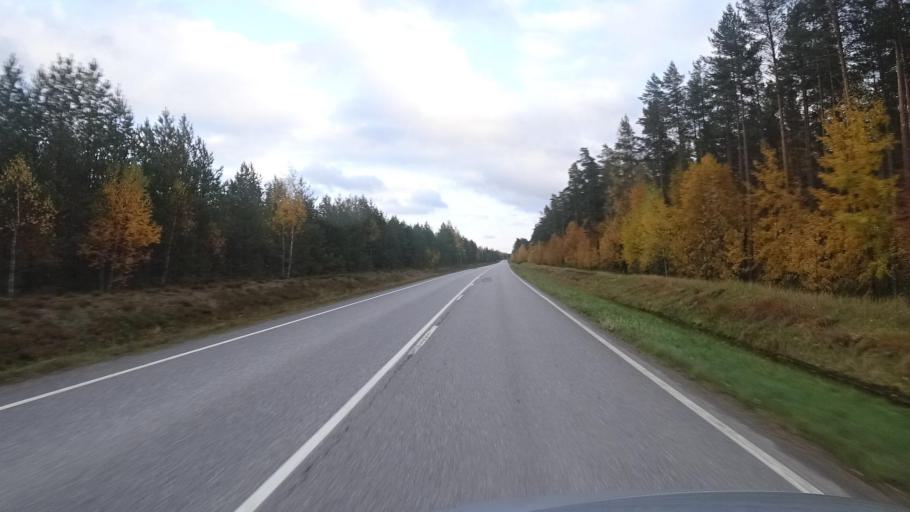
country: FI
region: Satakunta
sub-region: Pori
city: Vampula
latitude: 60.9740
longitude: 22.5940
